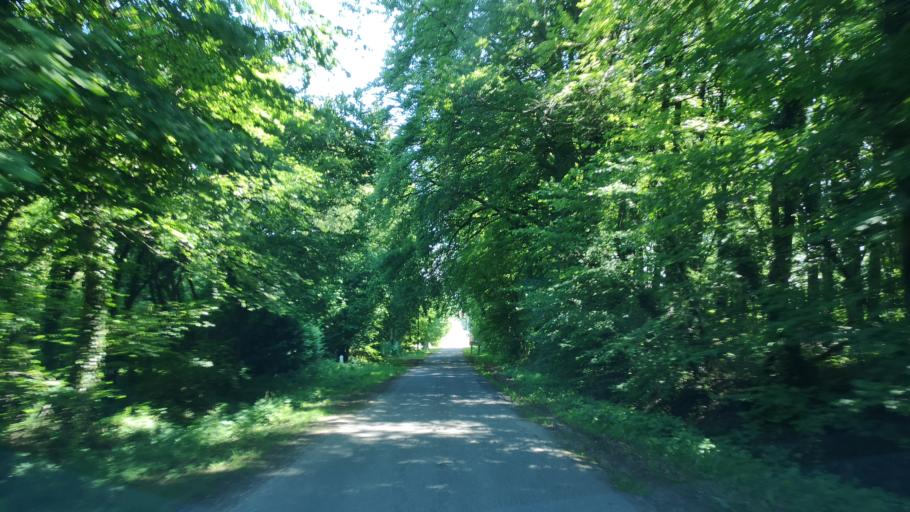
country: FR
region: Lorraine
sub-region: Departement de la Meuse
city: Vigneulles-les-Hattonchatel
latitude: 49.0327
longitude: 5.6495
